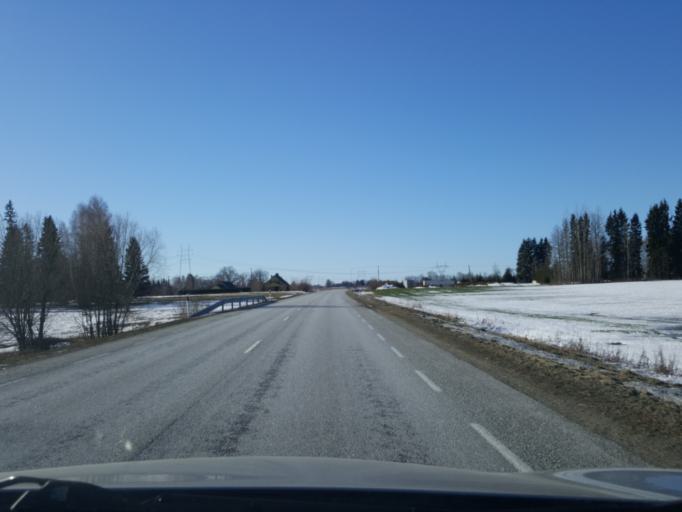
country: EE
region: Viljandimaa
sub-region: Viiratsi vald
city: Viiratsi
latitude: 58.3965
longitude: 25.6414
